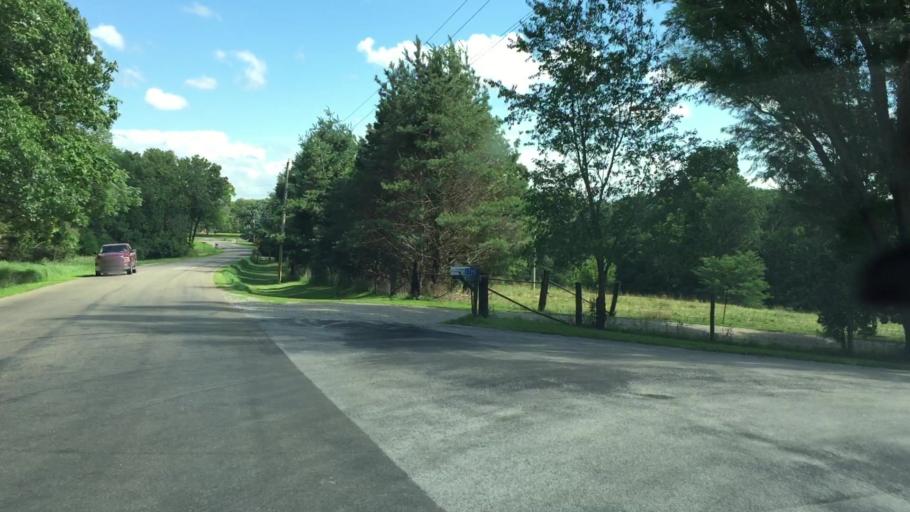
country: US
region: Iowa
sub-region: Johnson County
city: North Liberty
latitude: 41.8045
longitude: -91.6158
